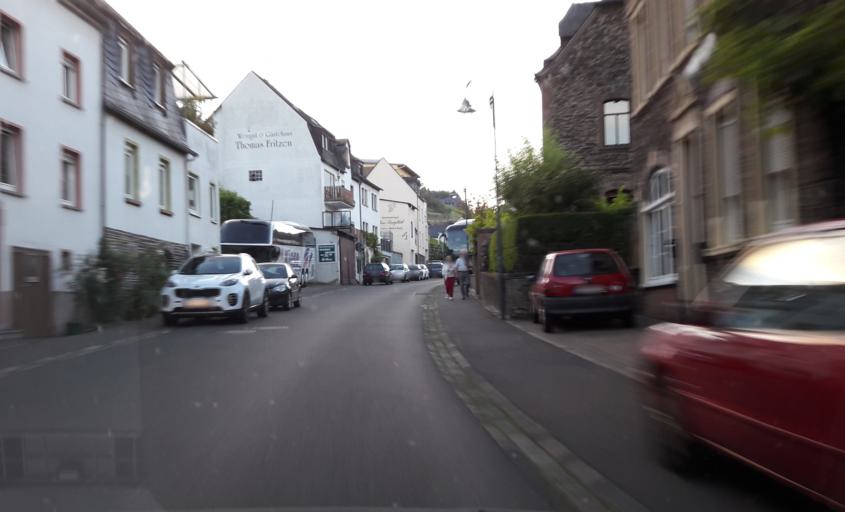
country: DE
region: Rheinland-Pfalz
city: Punderich
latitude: 50.0254
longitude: 7.1123
